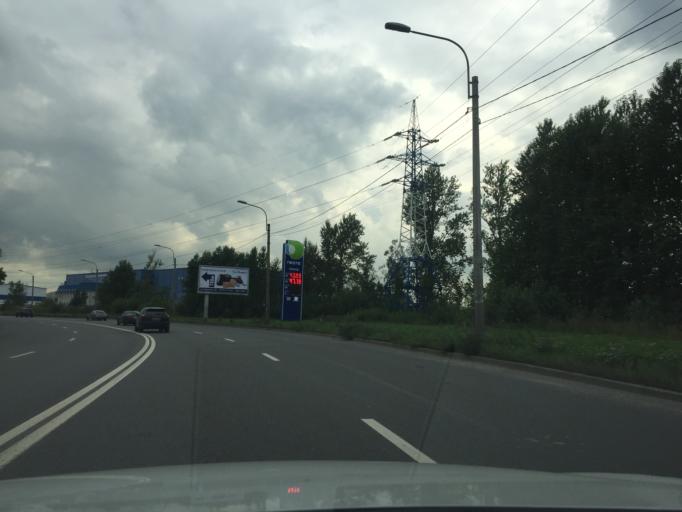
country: RU
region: St.-Petersburg
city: Avtovo
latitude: 59.8474
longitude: 30.2916
